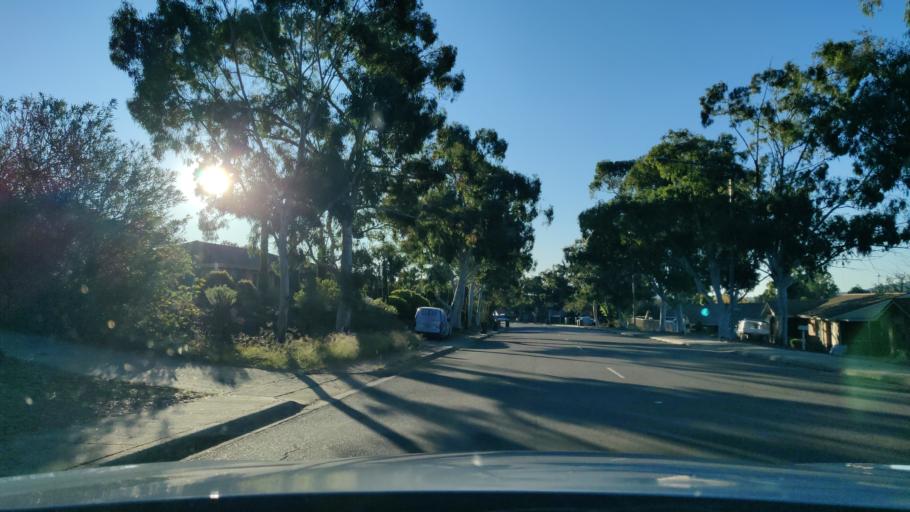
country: AU
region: Australian Capital Territory
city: Macarthur
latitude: -35.4471
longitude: 149.1201
